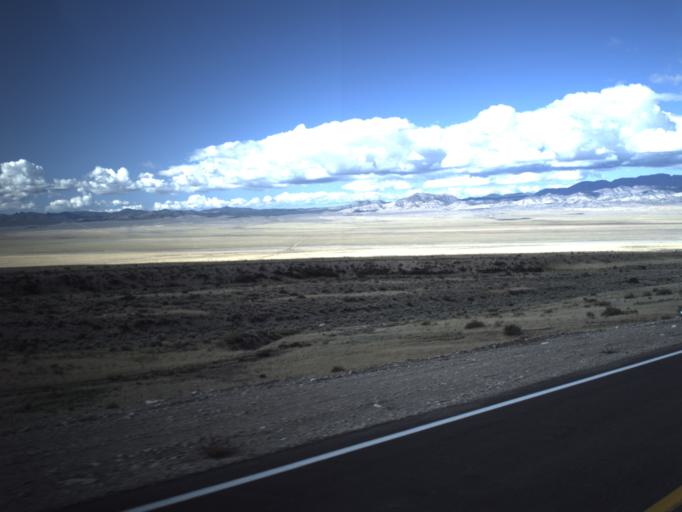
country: US
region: Utah
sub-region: Beaver County
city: Milford
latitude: 38.5057
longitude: -113.5986
